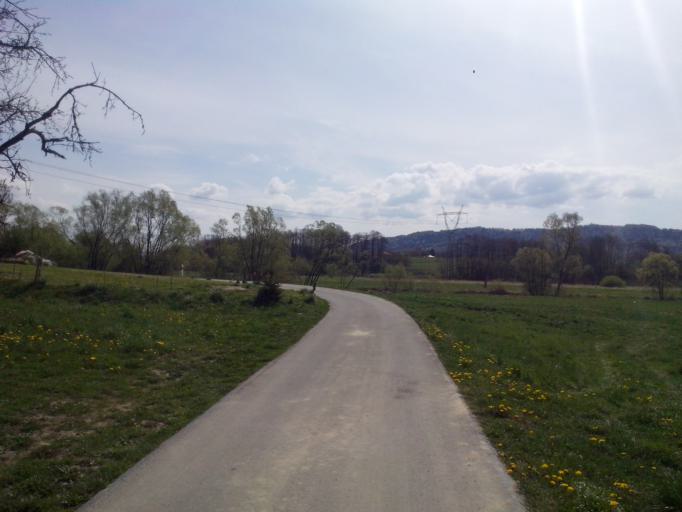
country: PL
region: Subcarpathian Voivodeship
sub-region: Powiat strzyzowski
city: Jawornik
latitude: 49.8081
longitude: 21.8630
